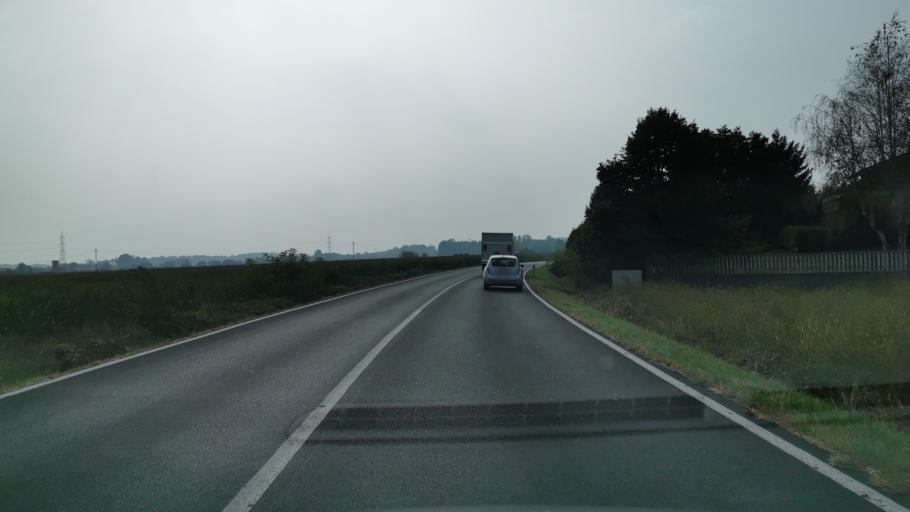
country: IT
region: Piedmont
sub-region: Provincia di Torino
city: San Benigno Canavese
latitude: 45.2255
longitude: 7.7602
